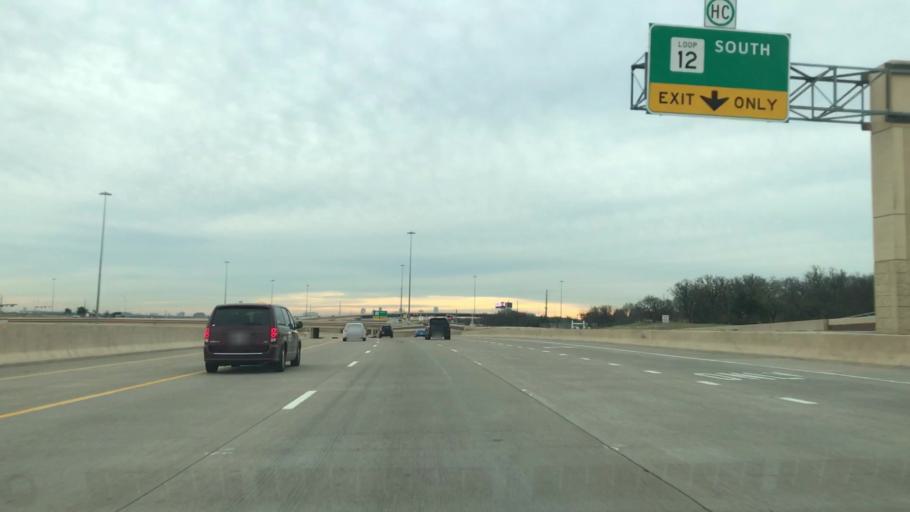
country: US
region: Texas
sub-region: Dallas County
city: Irving
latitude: 32.8507
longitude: -96.9204
